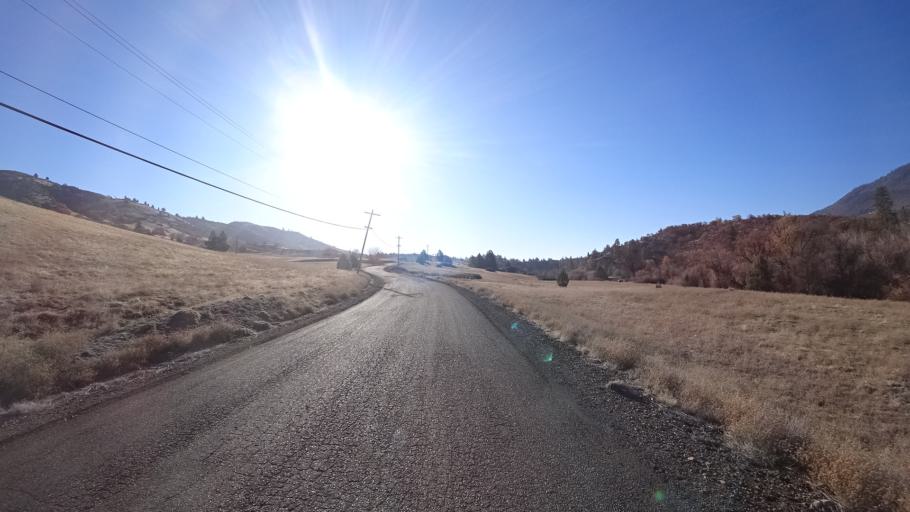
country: US
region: California
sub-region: Siskiyou County
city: Montague
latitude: 41.8894
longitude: -122.4805
